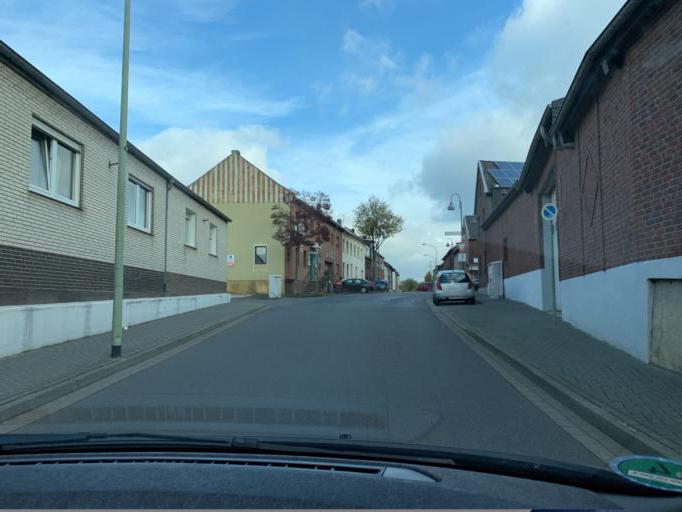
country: DE
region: North Rhine-Westphalia
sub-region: Regierungsbezirk Koln
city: Niederzier
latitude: 50.8571
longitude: 6.4558
